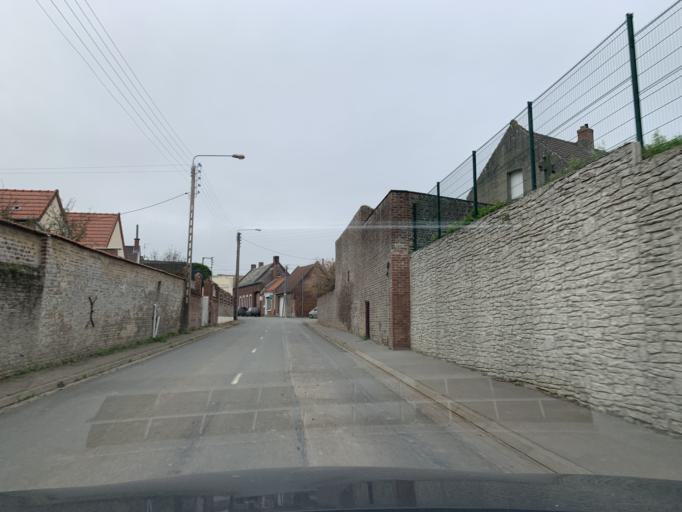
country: FR
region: Nord-Pas-de-Calais
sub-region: Departement du Pas-de-Calais
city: Oisy-le-Verger
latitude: 50.2506
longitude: 3.1262
